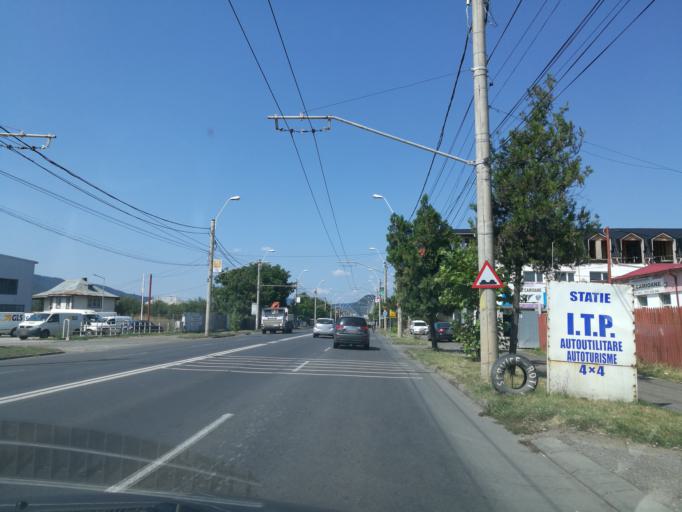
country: RO
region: Neamt
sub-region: Comuna Dumbrava Rosie
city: Cut
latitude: 46.9011
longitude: 26.4142
